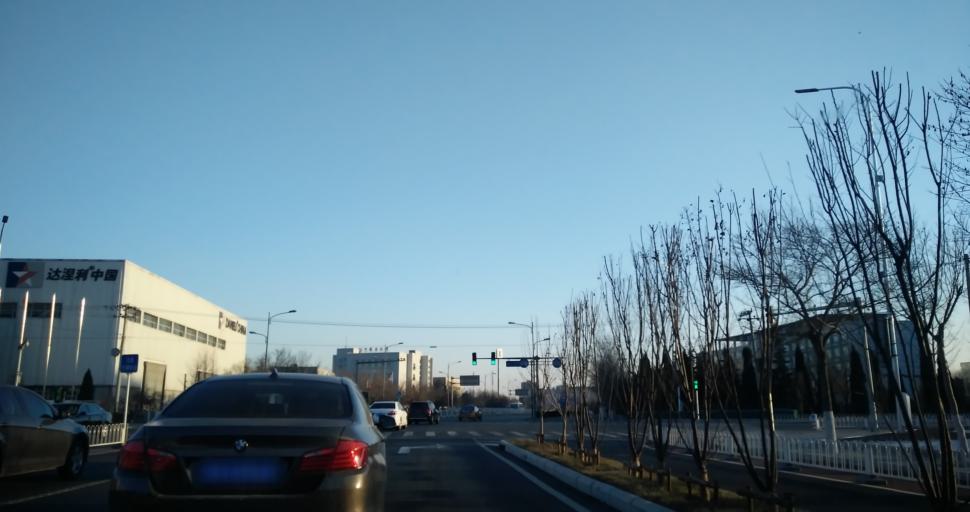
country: CN
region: Beijing
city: Jiugong
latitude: 39.7793
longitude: 116.5235
